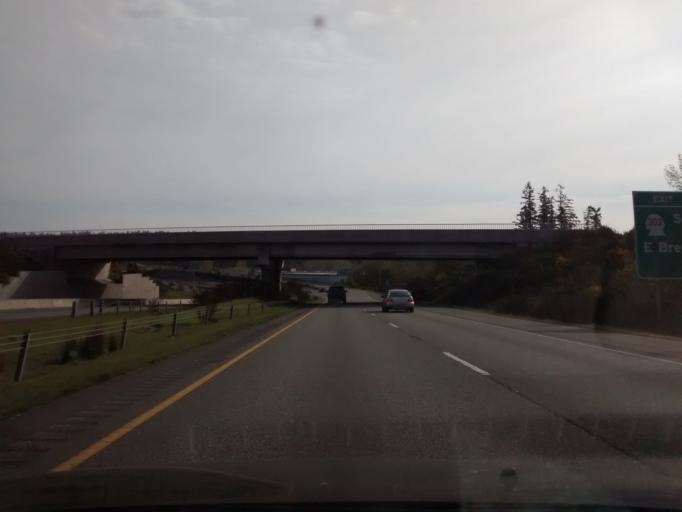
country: US
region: Washington
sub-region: Kitsap County
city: Silverdale
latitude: 47.6614
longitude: -122.6939
